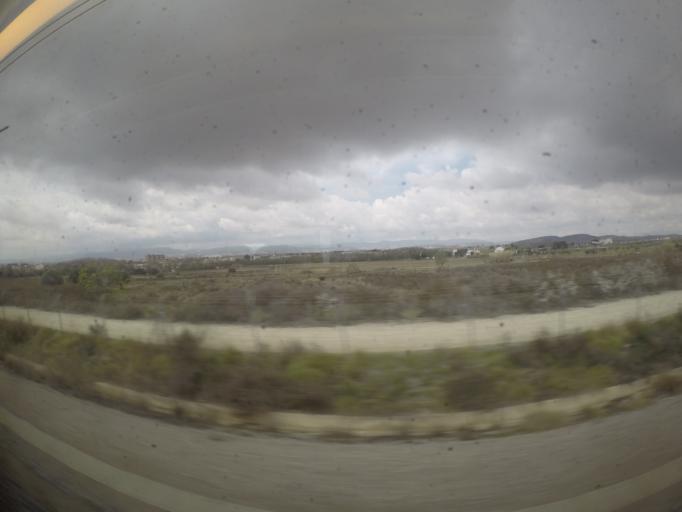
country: ES
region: Catalonia
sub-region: Provincia de Barcelona
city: Castellet
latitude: 41.3028
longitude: 1.6397
